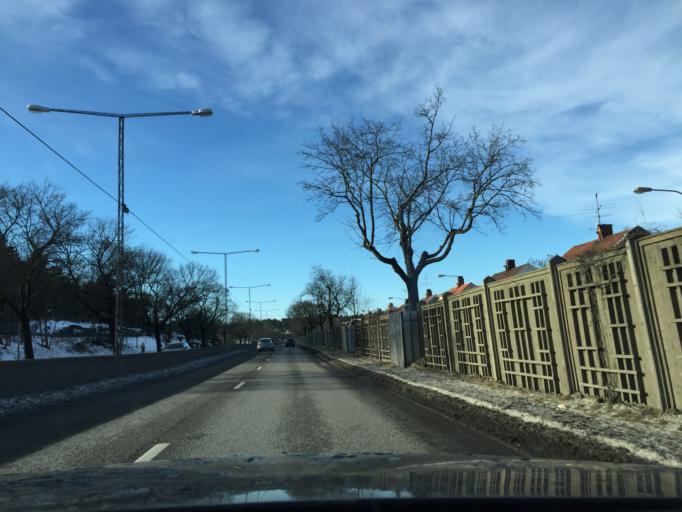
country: SE
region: Stockholm
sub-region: Stockholms Kommun
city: Bromma
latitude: 59.3425
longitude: 17.9183
